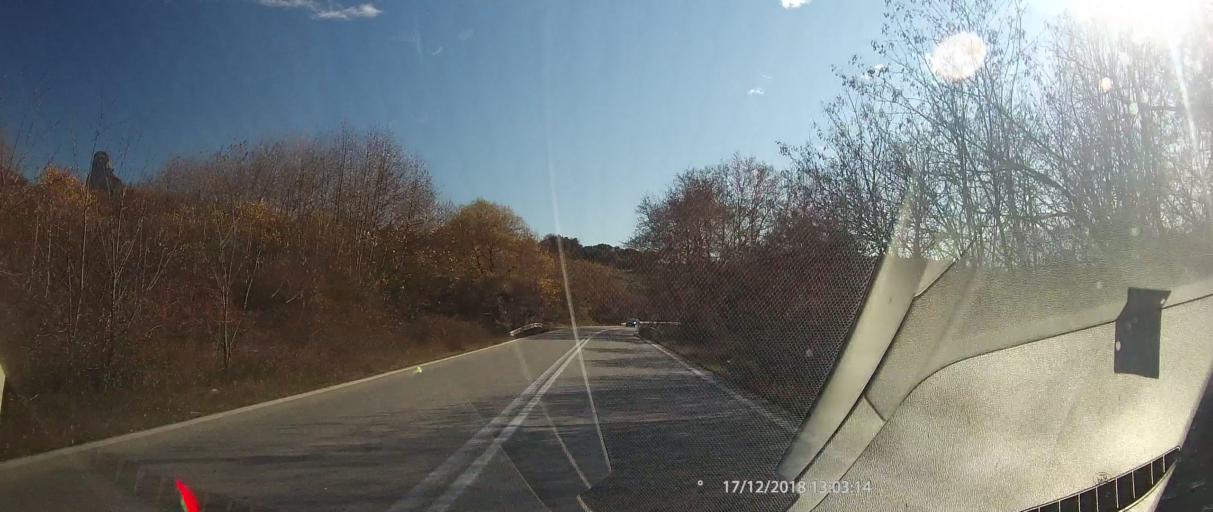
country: GR
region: Thessaly
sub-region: Trikala
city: Kastraki
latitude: 39.7152
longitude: 21.6011
